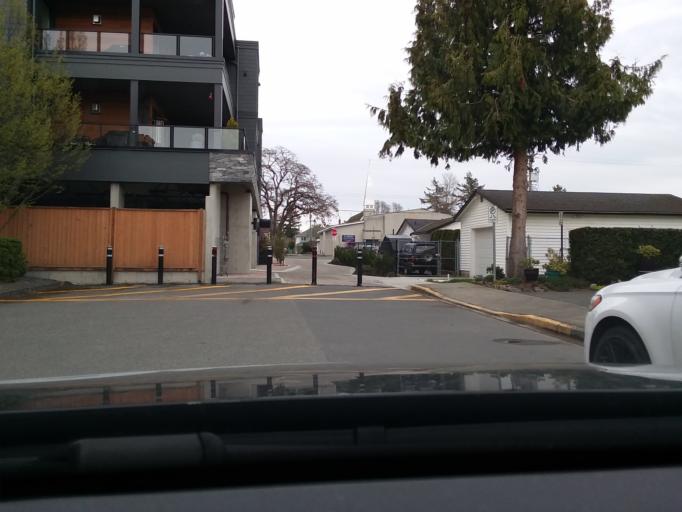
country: CA
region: British Columbia
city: North Saanich
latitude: 48.6468
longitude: -123.3999
